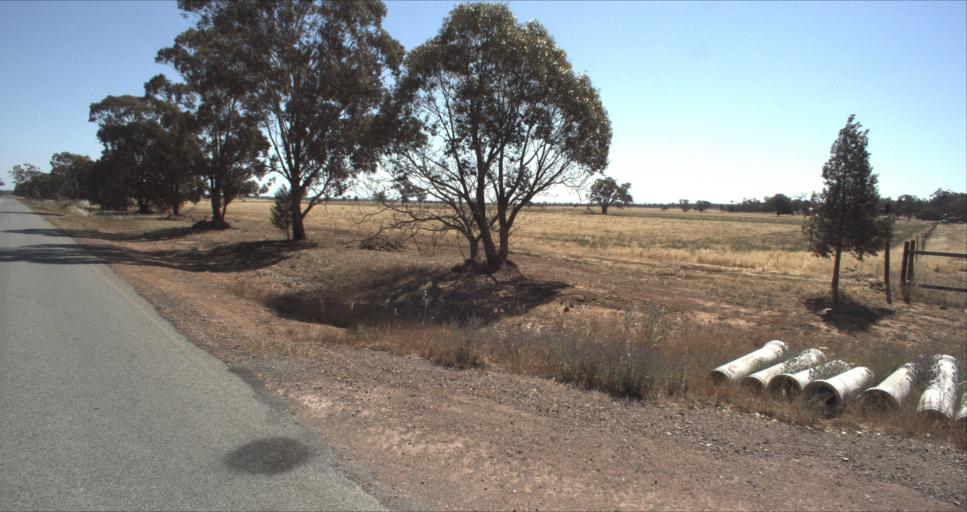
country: AU
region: New South Wales
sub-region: Leeton
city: Leeton
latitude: -34.4906
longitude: 146.4654
